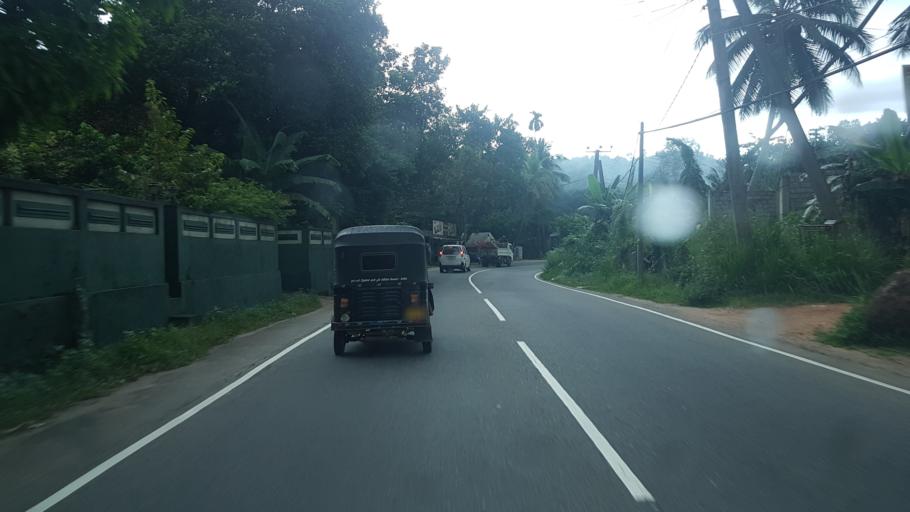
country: LK
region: Western
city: Hanwella Ihala
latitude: 6.9635
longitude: 80.2296
